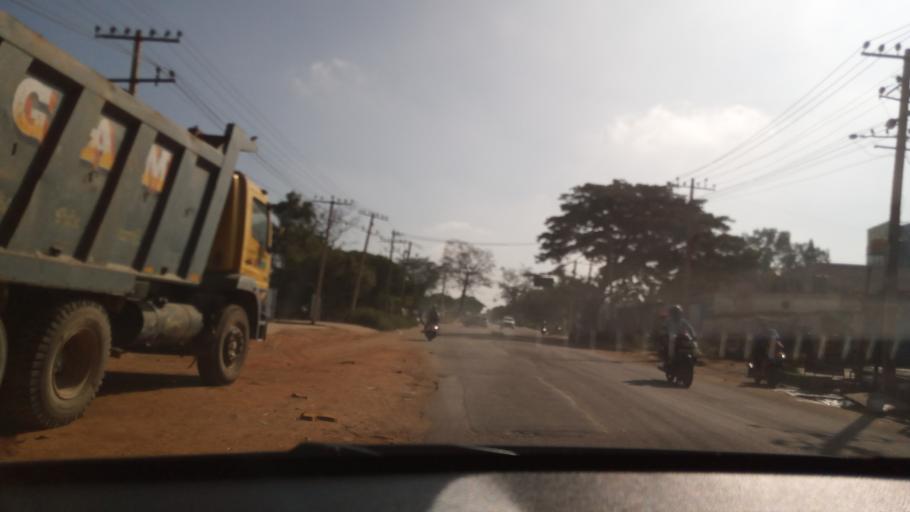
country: IN
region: Karnataka
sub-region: Bangalore Rural
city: Devanhalli
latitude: 13.2571
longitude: 77.7164
